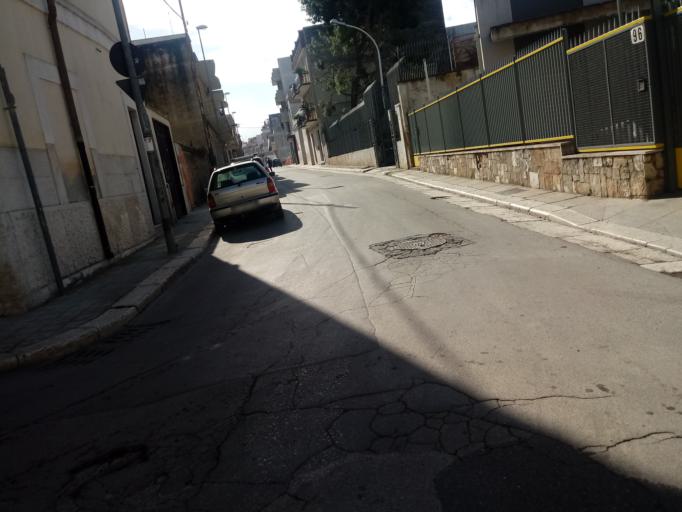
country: IT
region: Apulia
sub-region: Provincia di Barletta - Andria - Trani
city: Andria
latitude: 41.2213
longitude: 16.2957
